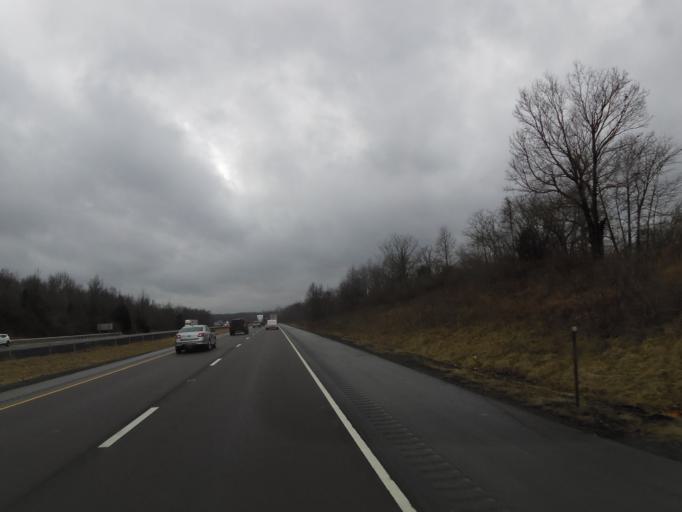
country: US
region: Illinois
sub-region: Williamson County
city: Marion
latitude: 37.7067
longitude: -88.9628
